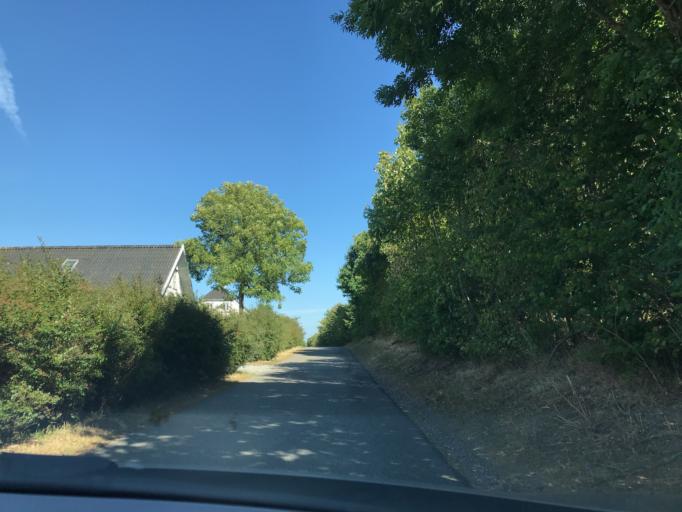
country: DK
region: South Denmark
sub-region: Kolding Kommune
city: Kolding
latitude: 55.5432
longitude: 9.4888
